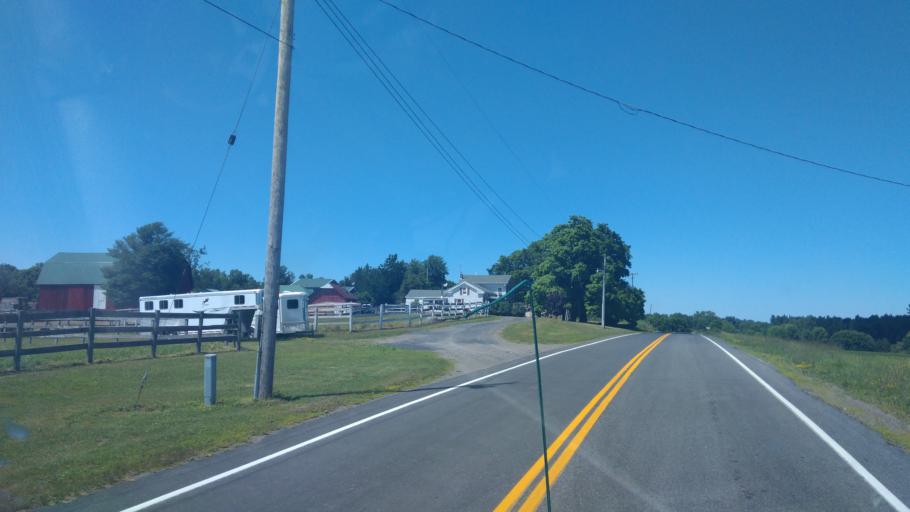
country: US
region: New York
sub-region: Wayne County
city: Lyons
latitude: 43.1356
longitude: -76.9597
